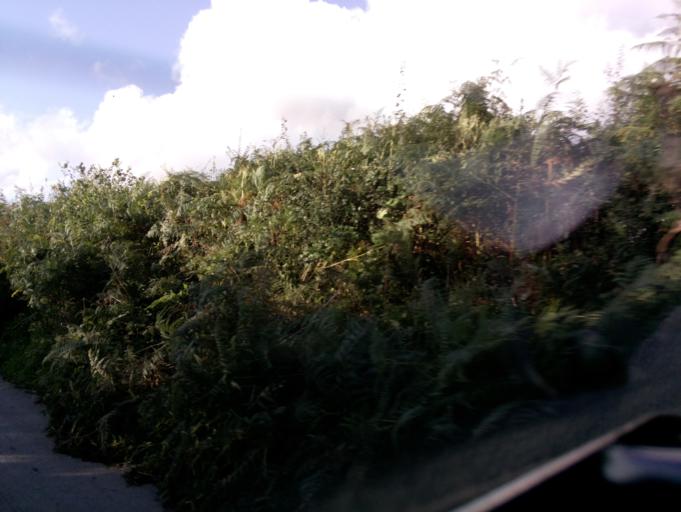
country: GB
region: England
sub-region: Devon
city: Totnes
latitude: 50.3525
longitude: -3.7196
